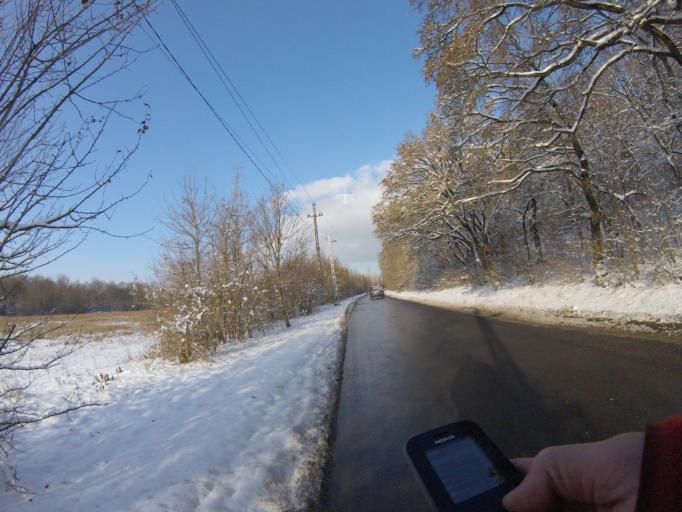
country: HU
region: Pest
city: Budakeszi
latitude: 47.4984
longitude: 18.9226
